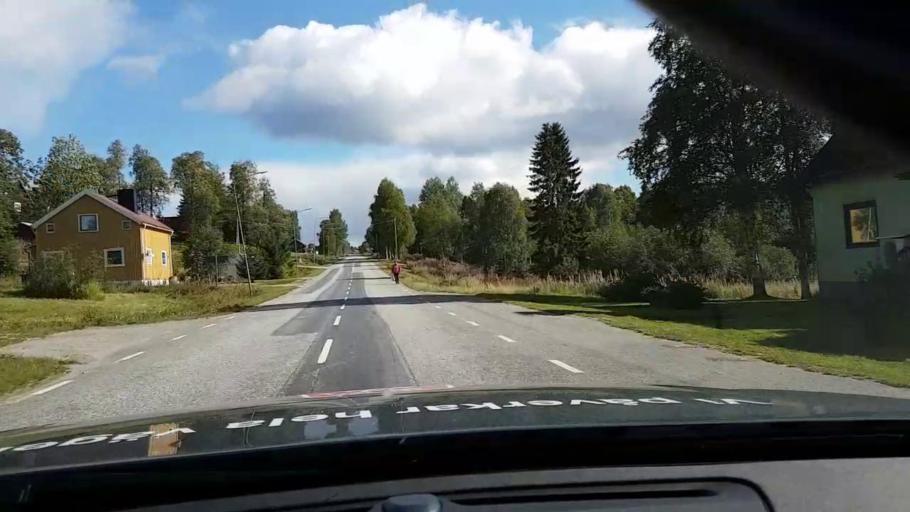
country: SE
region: Vaesterbotten
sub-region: Asele Kommun
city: Asele
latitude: 63.7875
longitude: 17.6453
